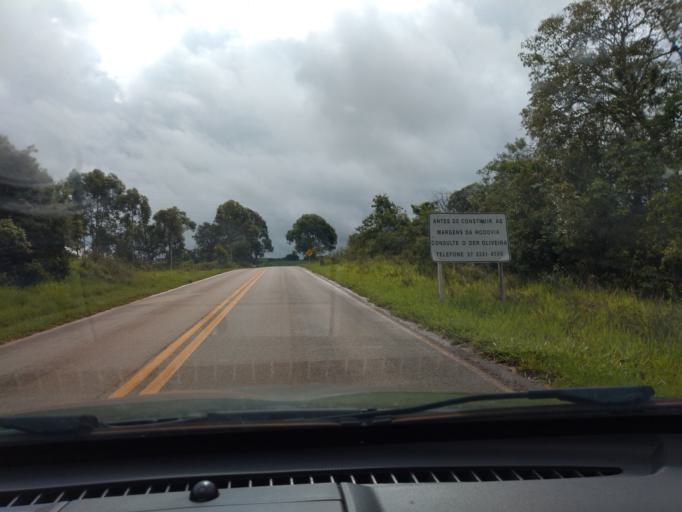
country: BR
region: Minas Gerais
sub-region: Lavras
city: Lavras
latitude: -21.5064
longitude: -44.9177
